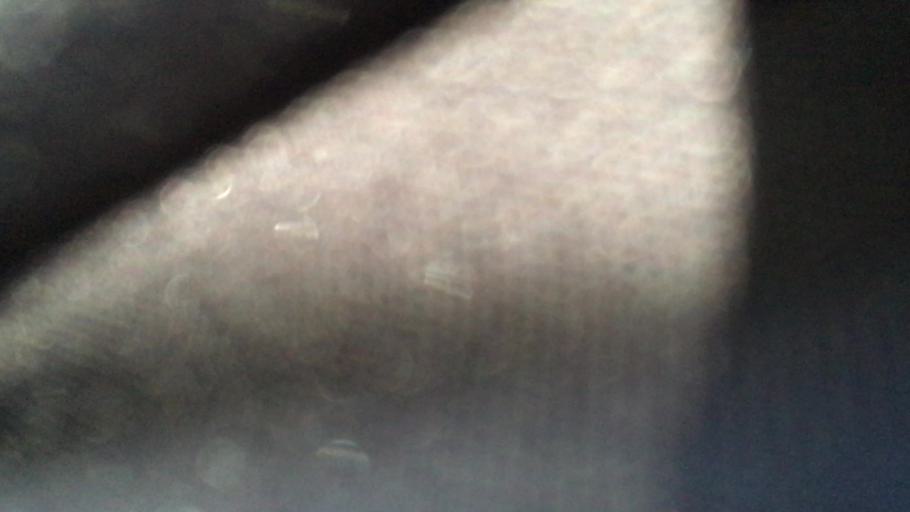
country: US
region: Maryland
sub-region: Somerset County
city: Princess Anne
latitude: 38.1412
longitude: -75.7003
